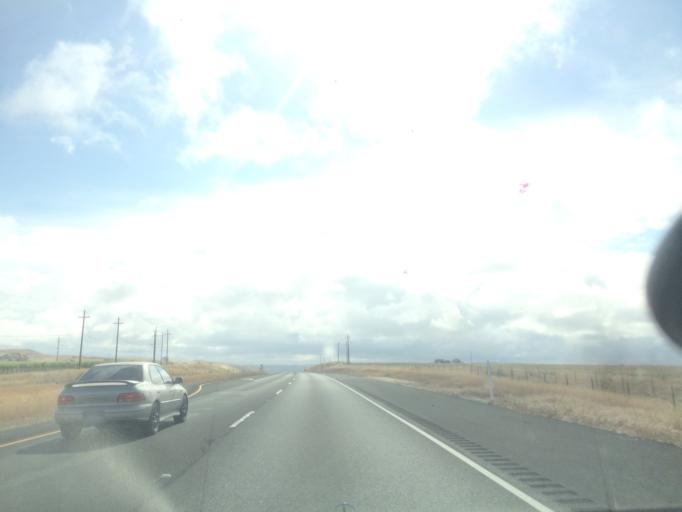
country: US
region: California
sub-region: San Luis Obispo County
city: Shandon
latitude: 35.6588
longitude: -120.4834
